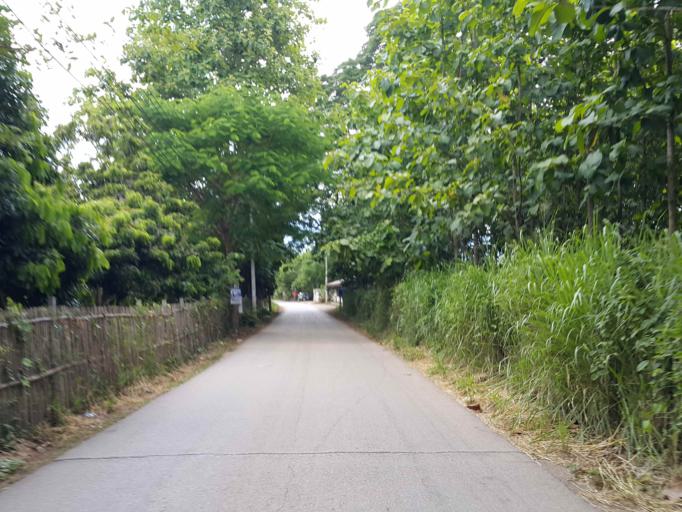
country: TH
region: Chiang Mai
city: Chiang Mai
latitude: 18.7397
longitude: 98.9891
